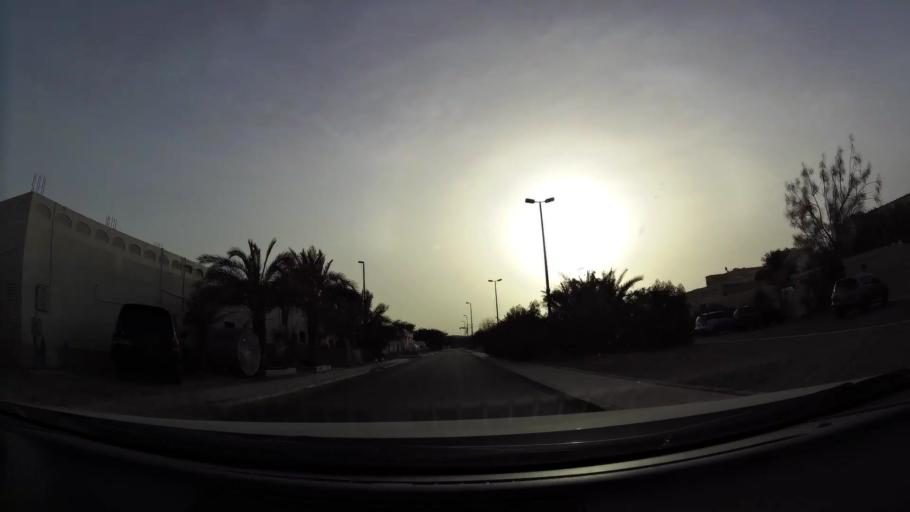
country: AE
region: Abu Dhabi
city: Al Ain
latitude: 24.2440
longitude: 55.7343
